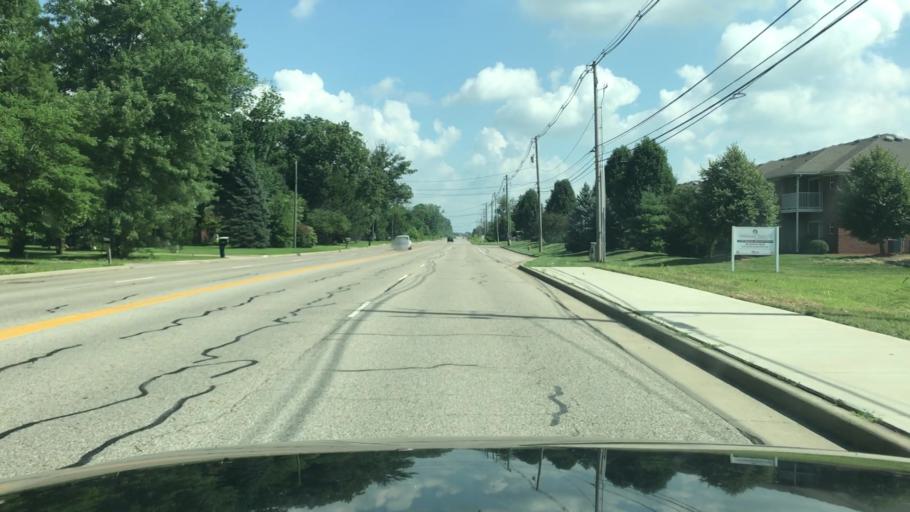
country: US
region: Indiana
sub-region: Vanderburgh County
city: Melody Hill
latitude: 38.0151
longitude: -87.4922
